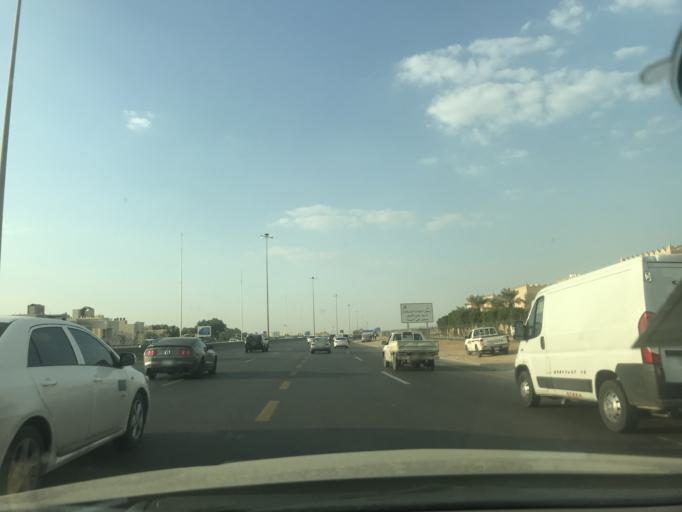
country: SA
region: Ar Riyad
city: Riyadh
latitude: 24.7424
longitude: 46.5868
